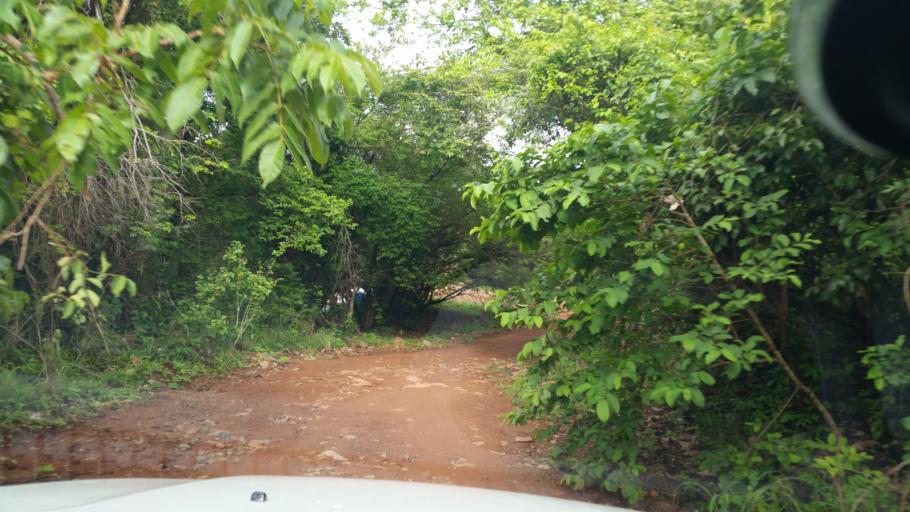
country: BR
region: Goias
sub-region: Porangatu
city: Porangatu
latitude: -13.9797
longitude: -49.2736
